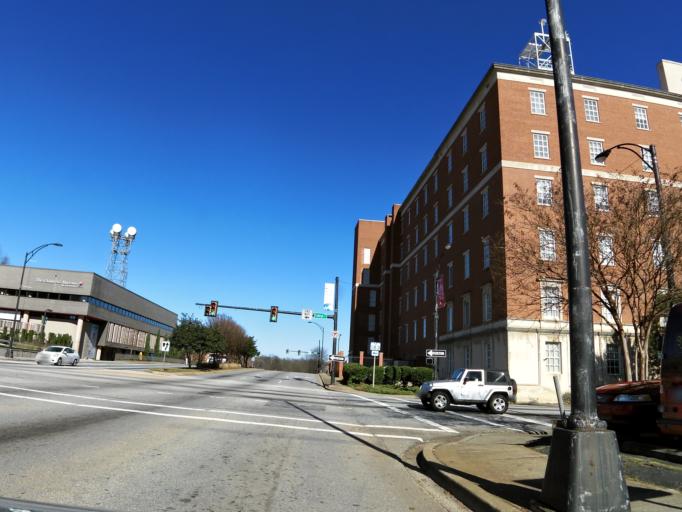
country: US
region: South Carolina
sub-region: Greenville County
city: Greenville
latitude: 34.8549
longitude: -82.4003
